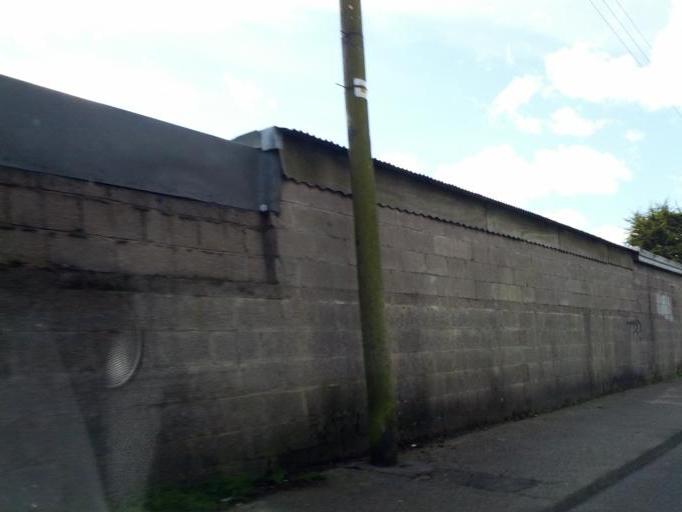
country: IE
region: Leinster
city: Clondalkin
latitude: 53.3257
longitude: -6.3877
